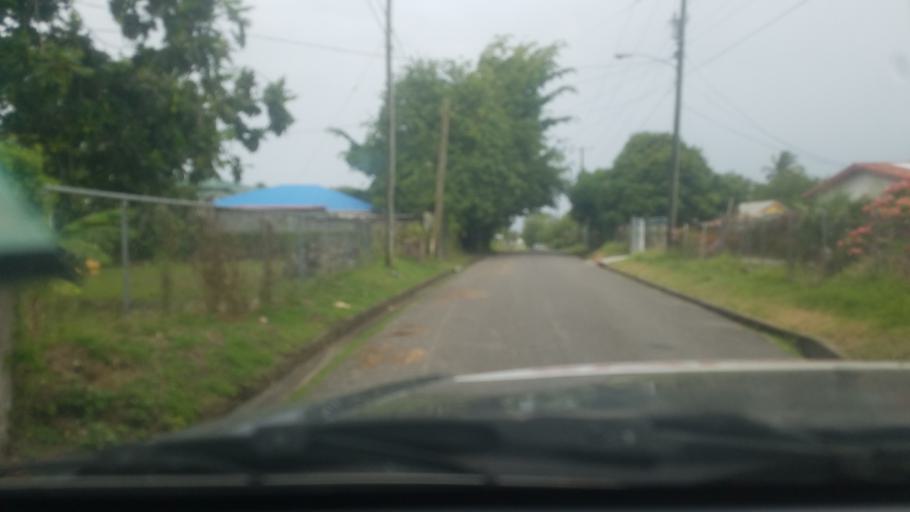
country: LC
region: Laborie Quarter
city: Laborie
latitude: 13.7565
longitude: -60.9802
